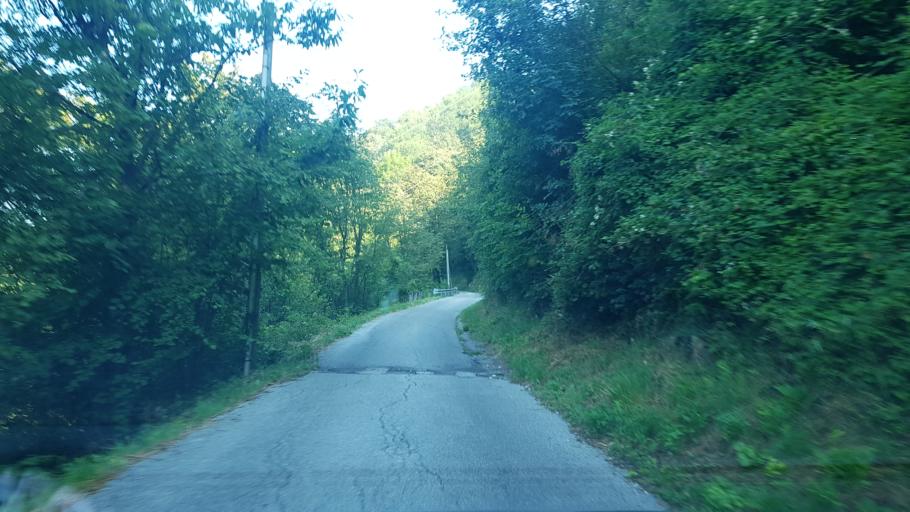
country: IT
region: Friuli Venezia Giulia
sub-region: Provincia di Udine
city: Nimis
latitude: 46.2315
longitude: 13.2472
